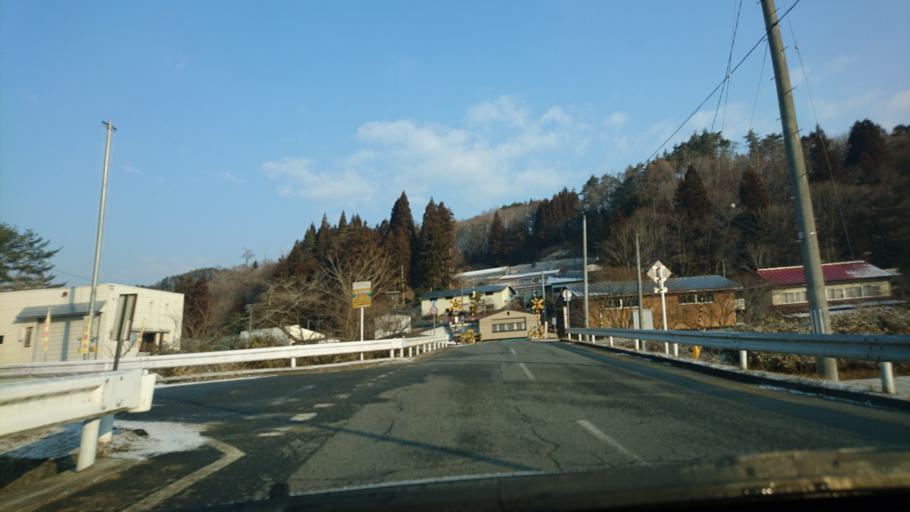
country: JP
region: Iwate
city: Ichinoseki
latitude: 38.9317
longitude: 141.3827
